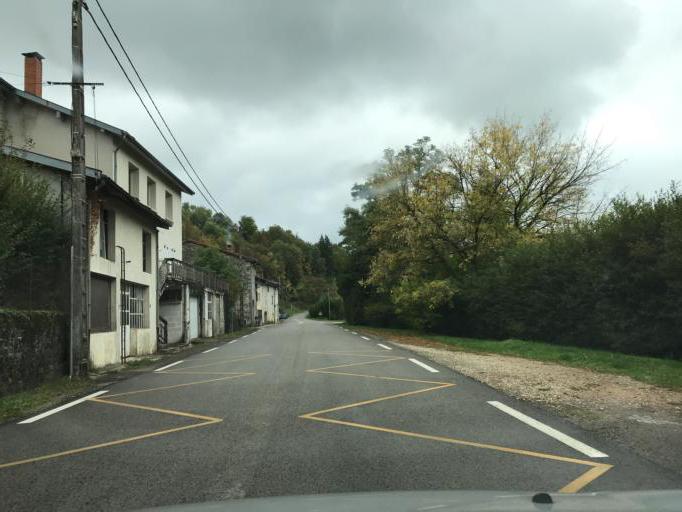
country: FR
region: Rhone-Alpes
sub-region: Departement de l'Ain
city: Coligny
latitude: 46.4005
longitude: 5.4526
